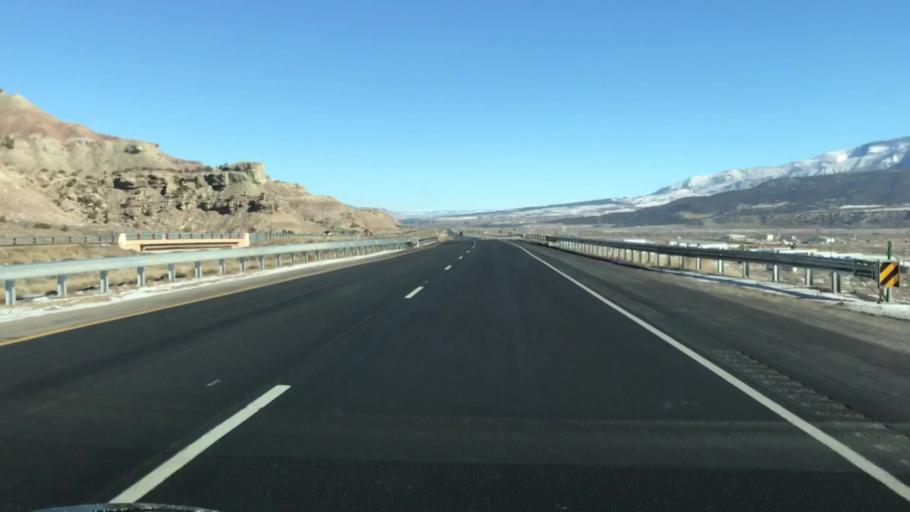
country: US
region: Colorado
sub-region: Garfield County
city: Parachute
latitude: 39.3992
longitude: -108.1168
